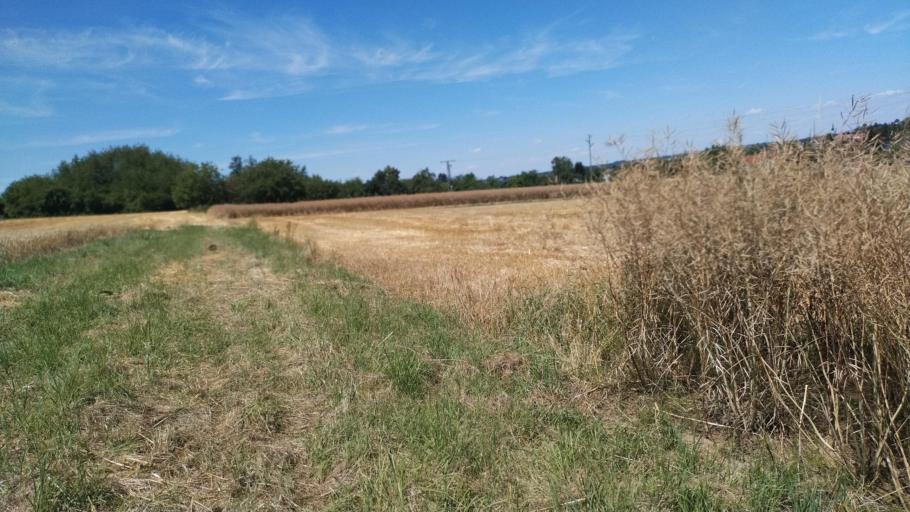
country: DE
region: Baden-Wuerttemberg
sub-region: Karlsruhe Region
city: Ubstadt-Weiher
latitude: 49.1531
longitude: 8.6299
